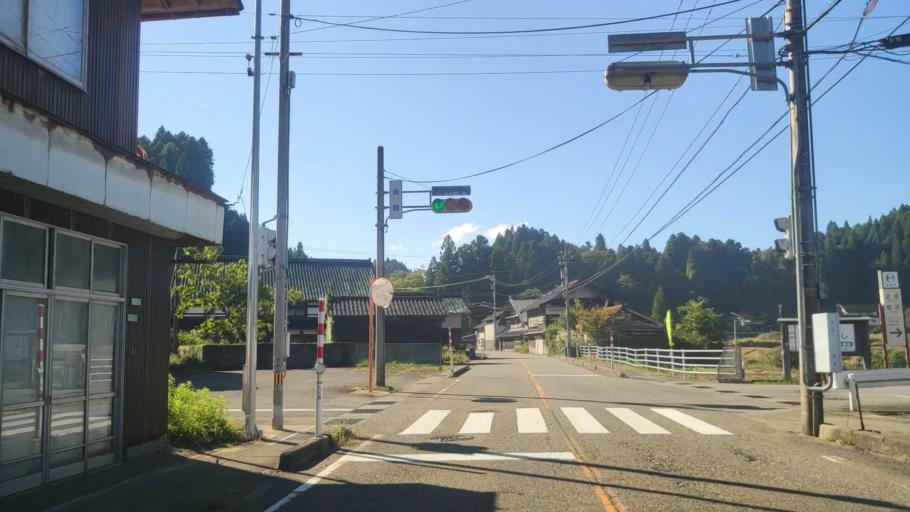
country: JP
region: Ishikawa
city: Nanao
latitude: 37.2817
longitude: 137.0408
